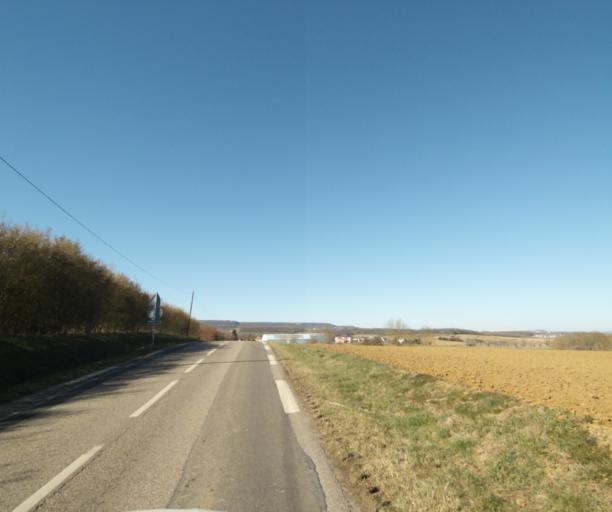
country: FR
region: Lorraine
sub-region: Departement de Meurthe-et-Moselle
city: Fleville-devant-Nancy
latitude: 48.6268
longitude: 6.2163
